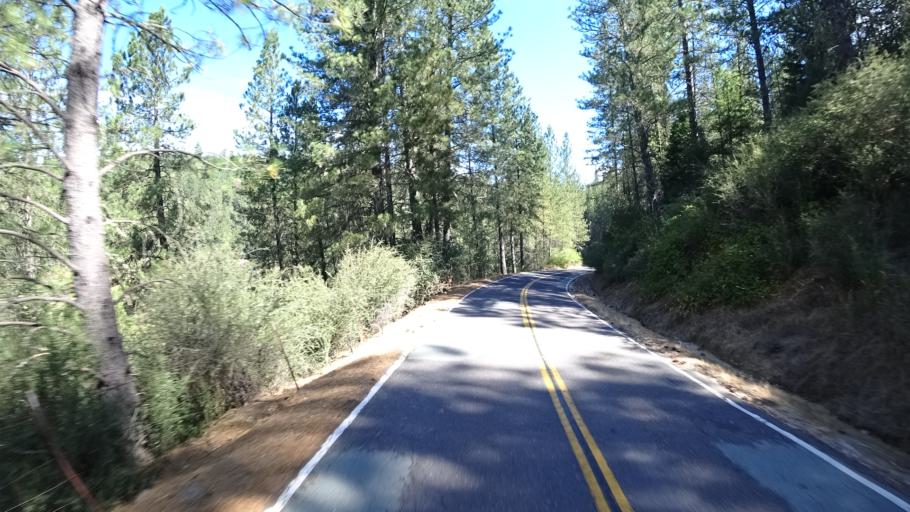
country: US
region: California
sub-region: Amador County
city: Pioneer
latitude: 38.3633
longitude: -120.5014
